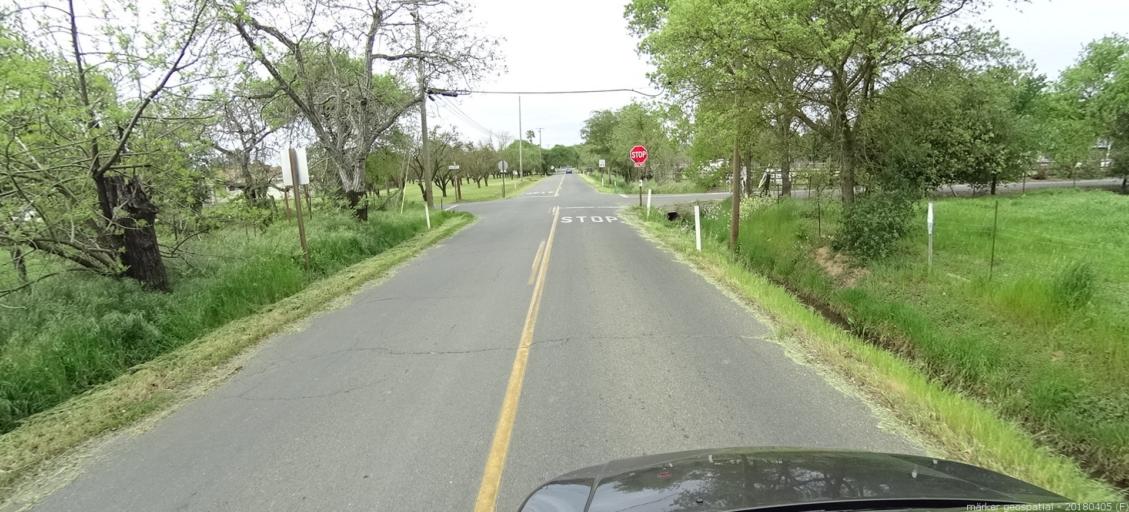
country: US
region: California
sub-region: Sacramento County
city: Galt
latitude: 38.2547
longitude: -121.3256
